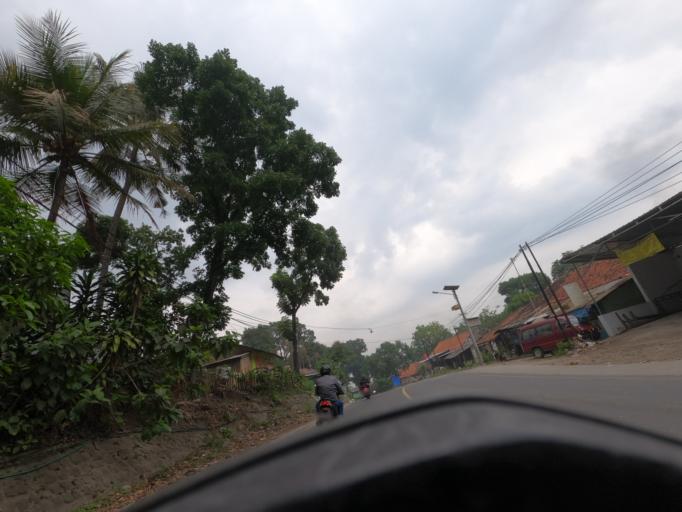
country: ID
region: West Java
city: Padalarang
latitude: -6.8327
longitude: 107.4380
